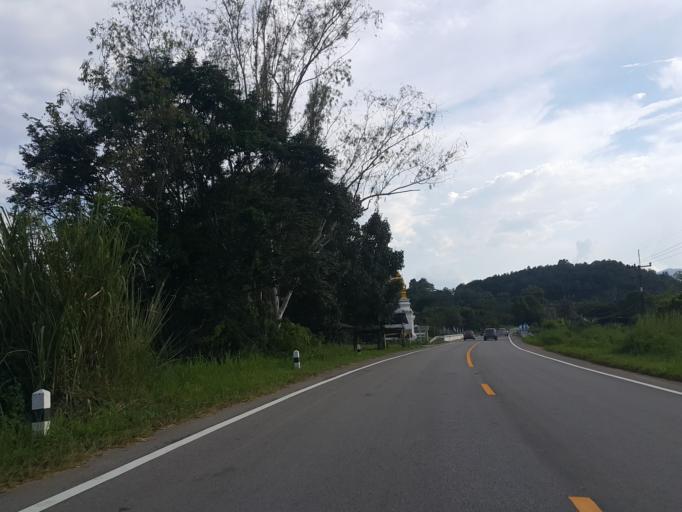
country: TH
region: Chiang Mai
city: Phrao
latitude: 19.2149
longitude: 99.1817
